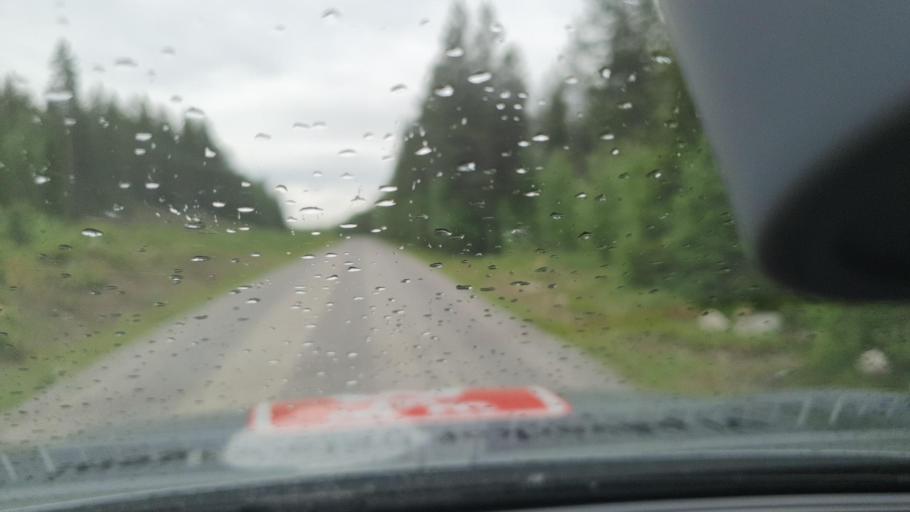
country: SE
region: Norrbotten
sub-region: Kalix Kommun
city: Rolfs
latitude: 66.0545
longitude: 23.0271
